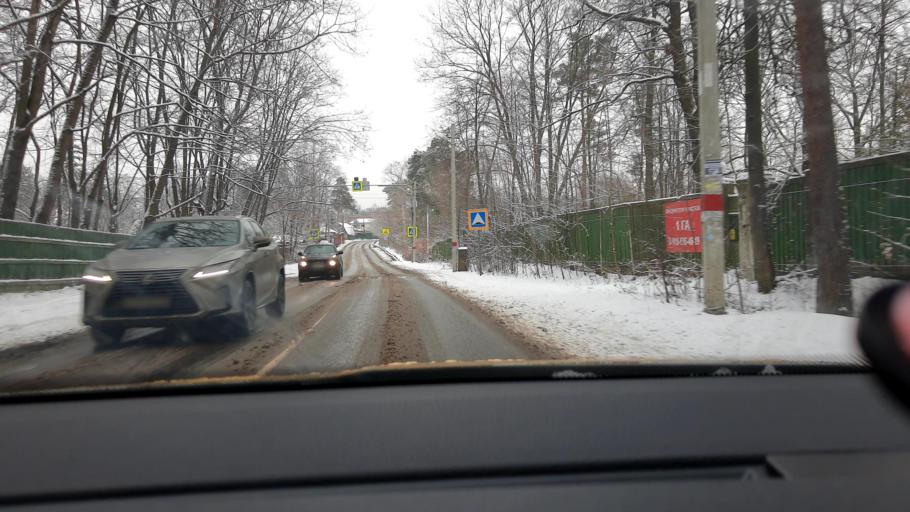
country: RU
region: Moskovskaya
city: Mamontovka
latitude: 55.9727
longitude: 37.8238
